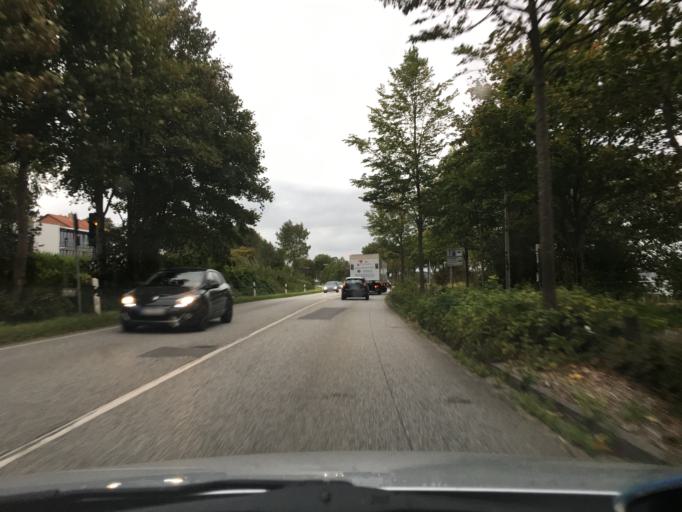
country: DE
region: Schleswig-Holstein
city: Eckernforde
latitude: 54.4570
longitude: 9.8466
